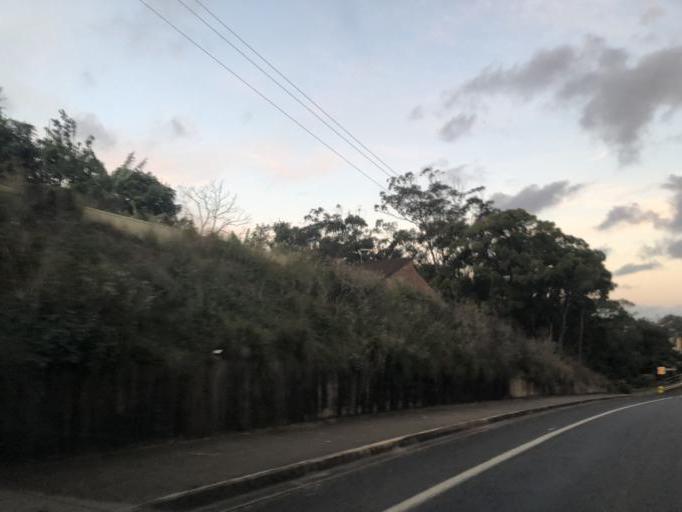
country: AU
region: New South Wales
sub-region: Coffs Harbour
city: Woolgoolga
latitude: -30.1078
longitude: 153.1895
